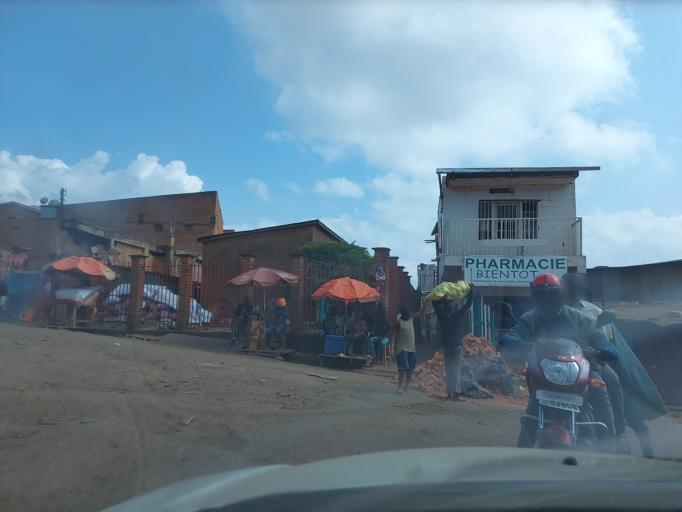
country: CD
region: South Kivu
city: Bukavu
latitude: -2.5223
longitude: 28.8528
